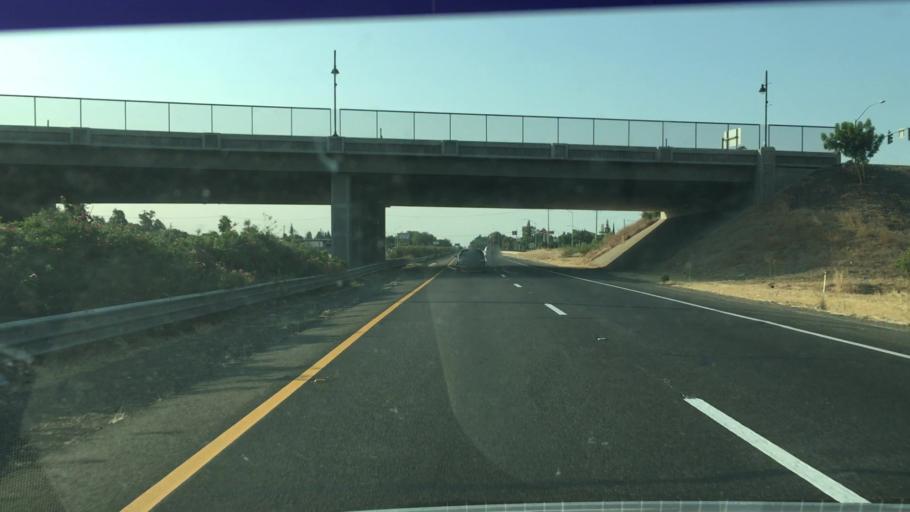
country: US
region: California
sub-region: Sacramento County
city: Galt
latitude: 38.2549
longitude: -121.2940
